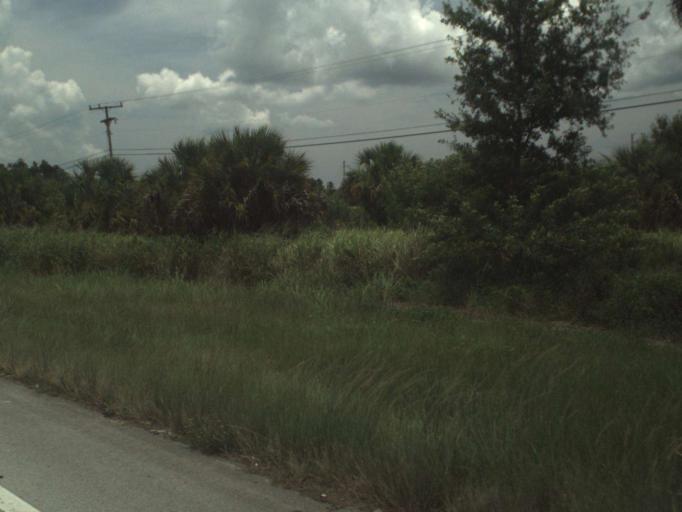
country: US
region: Florida
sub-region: Saint Lucie County
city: Lakewood Park
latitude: 27.5031
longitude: -80.3985
